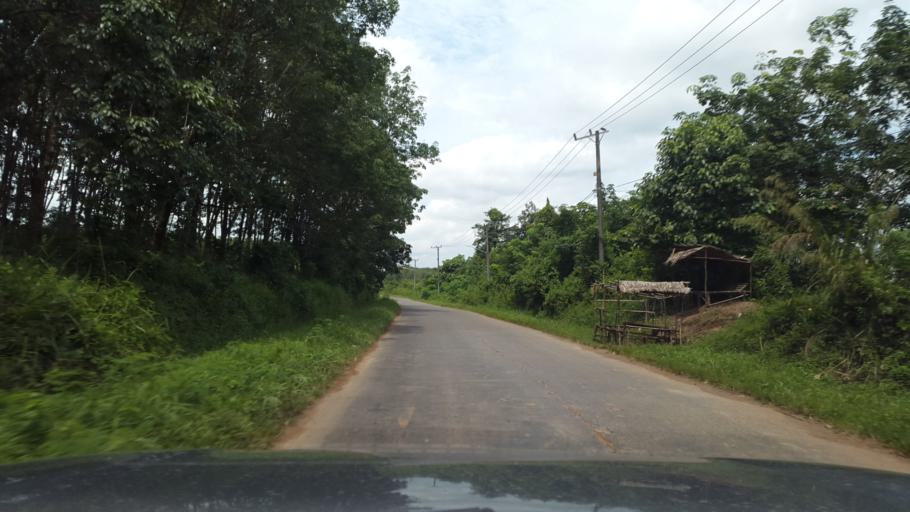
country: ID
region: South Sumatra
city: Gunungmegang Dalam
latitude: -3.3556
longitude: 103.9283
